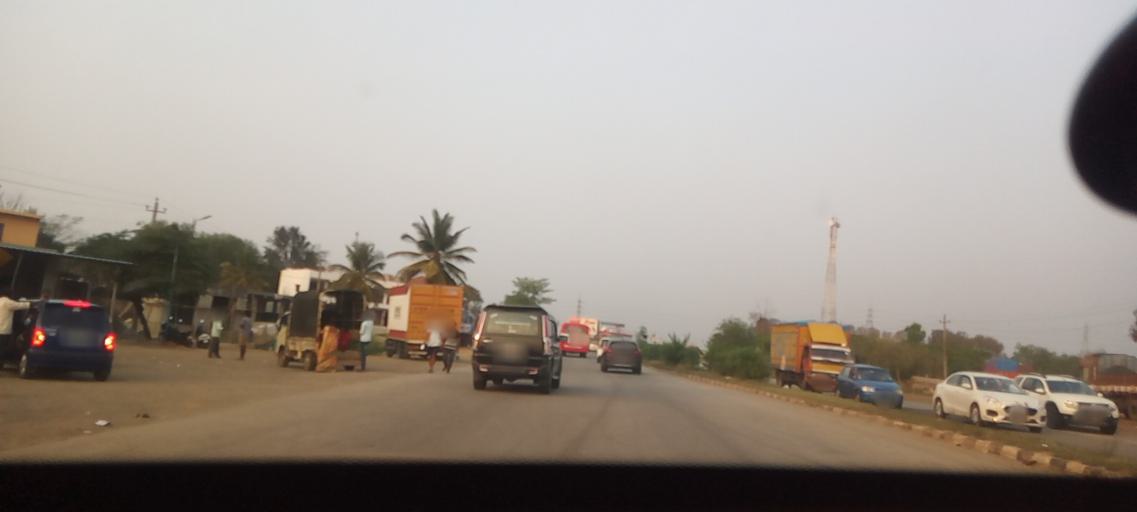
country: IN
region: Karnataka
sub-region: Tumkur
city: Kunigal
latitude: 13.0324
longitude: 77.0835
